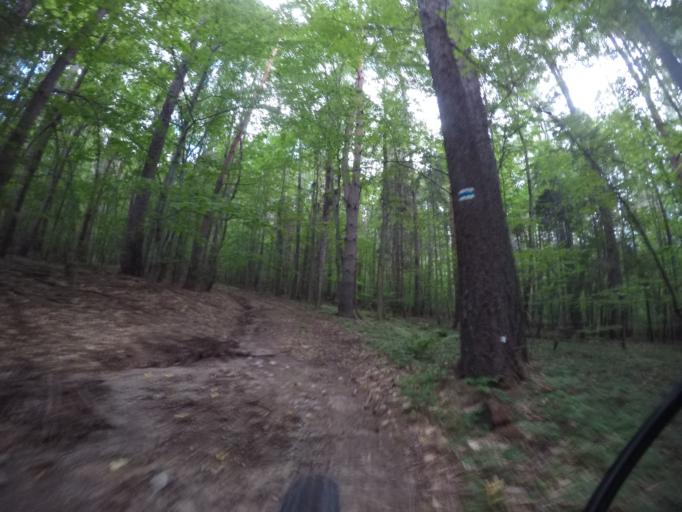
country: SK
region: Kosicky
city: Gelnica
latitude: 48.9241
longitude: 21.0314
